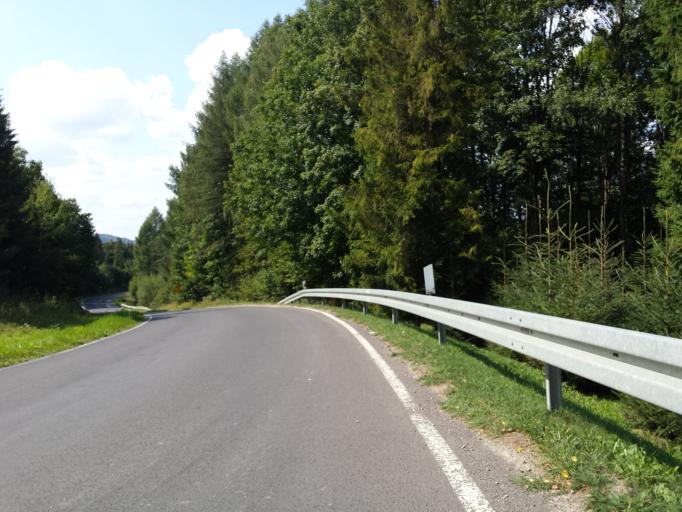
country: PL
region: Subcarpathian Voivodeship
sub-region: Powiat leski
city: Cisna
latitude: 49.1901
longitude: 22.3811
